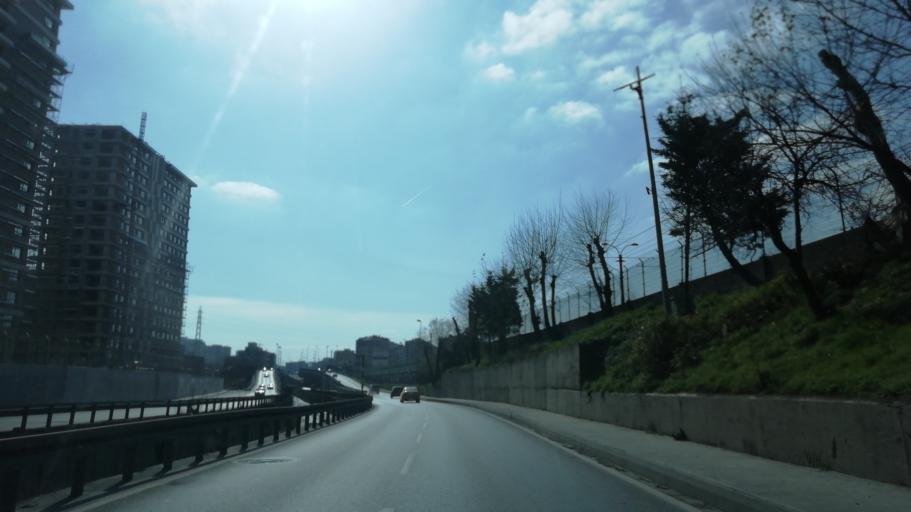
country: TR
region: Istanbul
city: merter keresteciler
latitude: 41.0241
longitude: 28.8993
